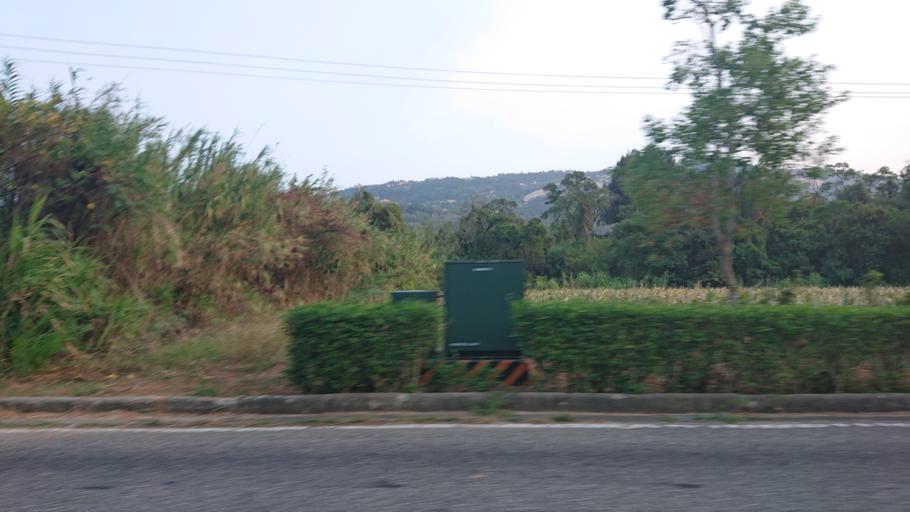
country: TW
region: Fukien
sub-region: Kinmen
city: Jincheng
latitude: 24.4763
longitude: 118.4175
